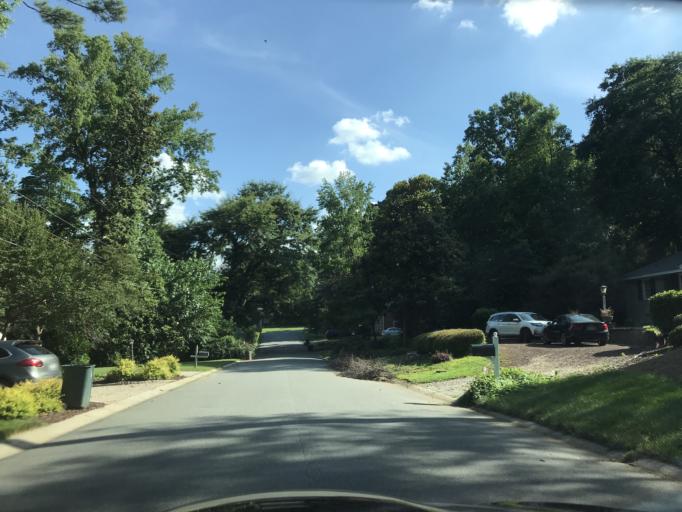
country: US
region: North Carolina
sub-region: Wake County
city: West Raleigh
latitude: 35.8315
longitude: -78.6728
